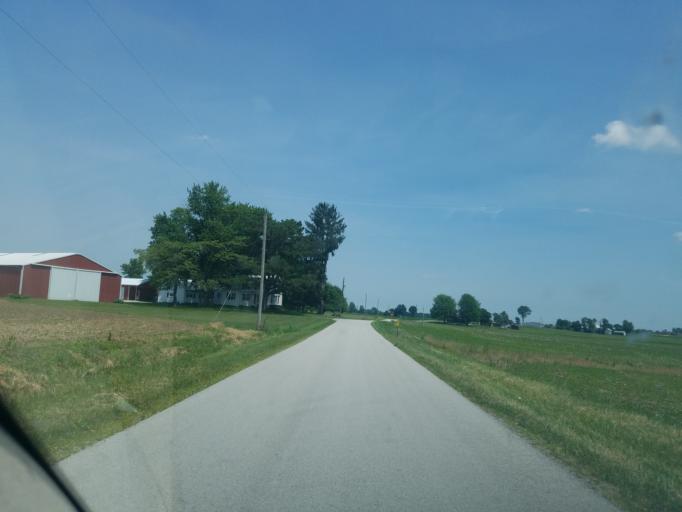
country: US
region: Ohio
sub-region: Wyandot County
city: Carey
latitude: 40.9524
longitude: -83.4896
